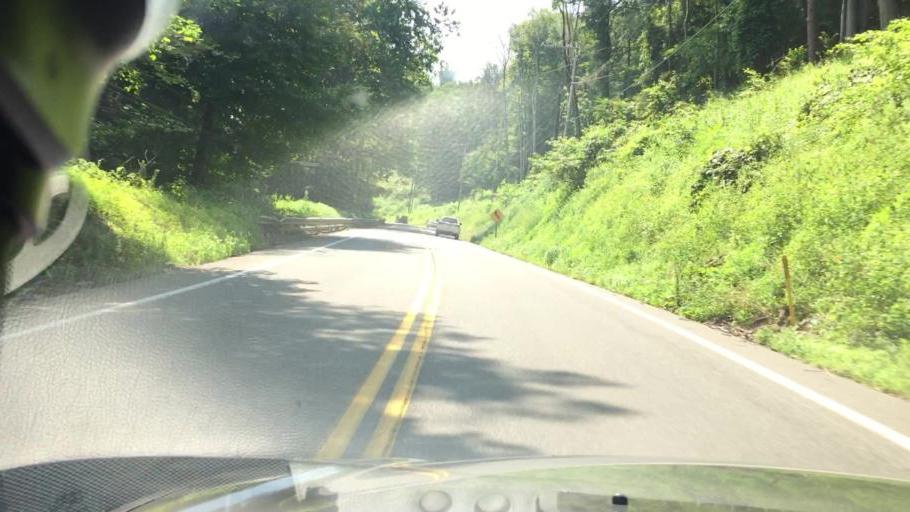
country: US
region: Pennsylvania
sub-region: Columbia County
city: Catawissa
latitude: 40.9370
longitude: -76.4561
